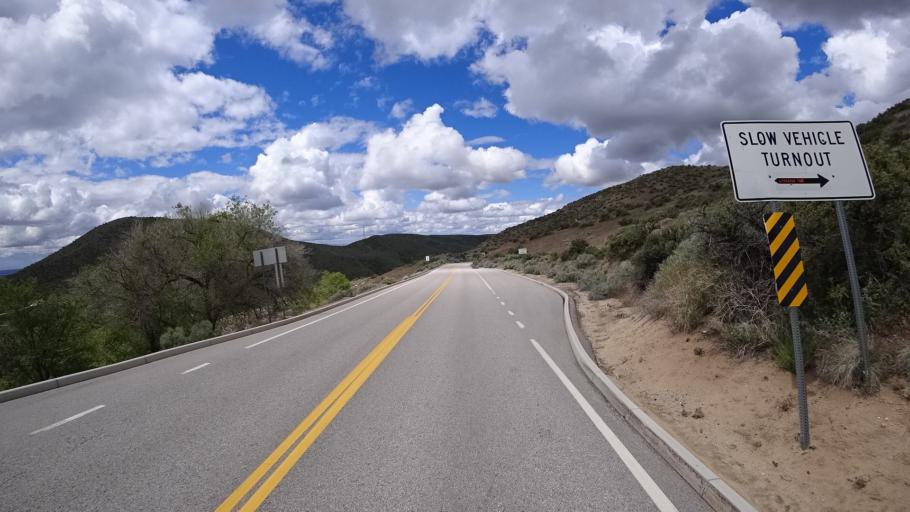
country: US
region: Idaho
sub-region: Ada County
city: Boise
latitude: 43.6896
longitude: -116.1829
